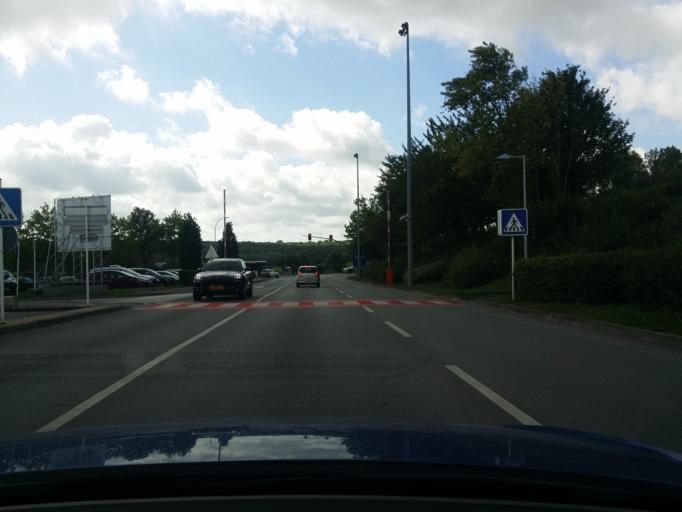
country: LU
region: Luxembourg
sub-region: Canton de Luxembourg
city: Bertrange
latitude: 49.6018
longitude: 6.0623
